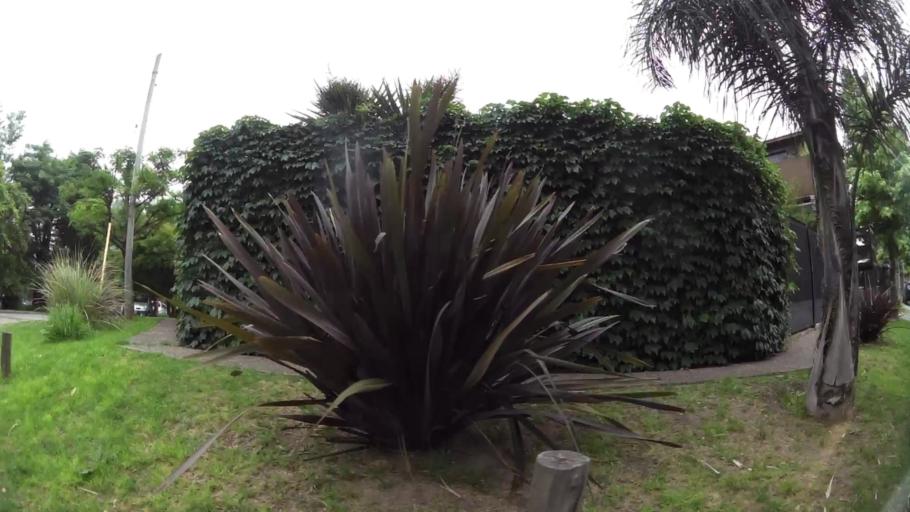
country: AR
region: Buenos Aires
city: San Justo
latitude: -34.7113
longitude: -58.5347
